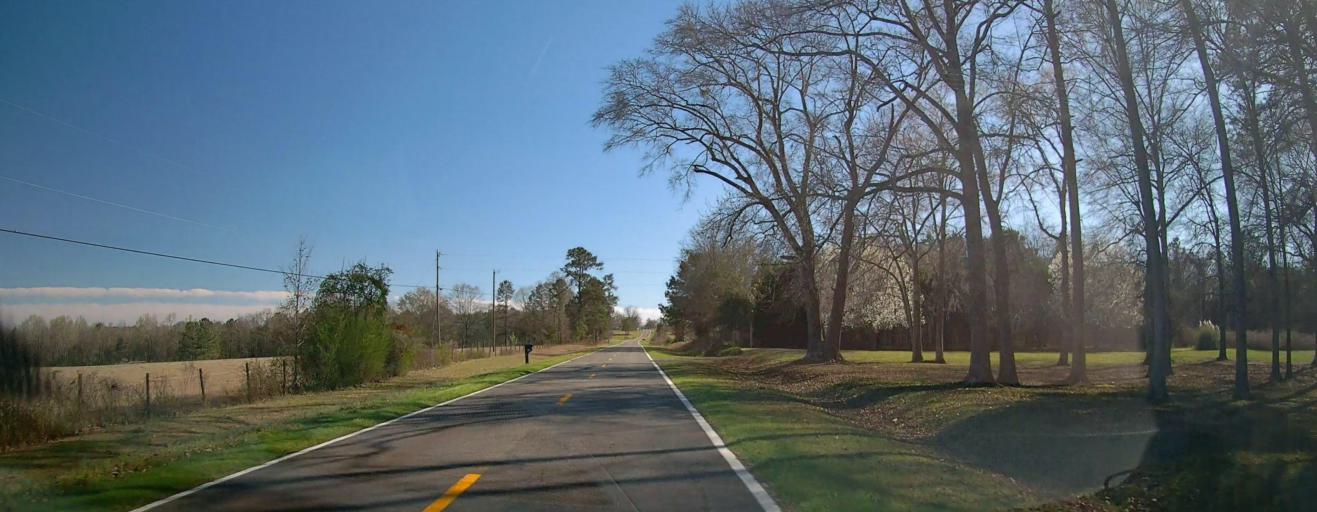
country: US
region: Georgia
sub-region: Peach County
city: Fort Valley
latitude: 32.6412
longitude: -83.8989
